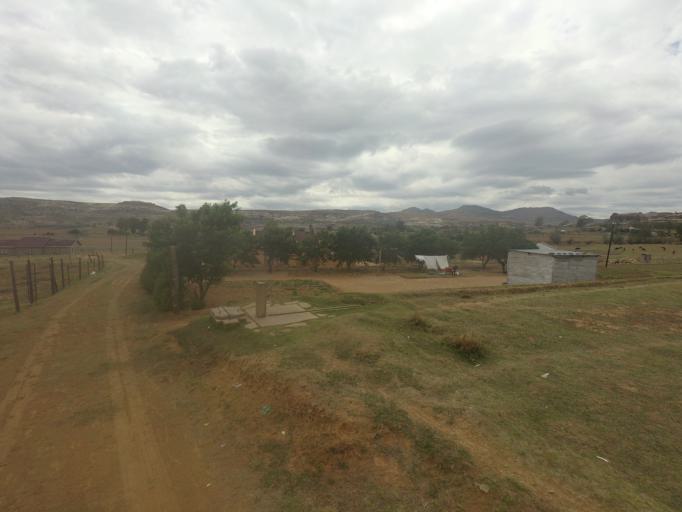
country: LS
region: Leribe
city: Leribe
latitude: -29.0273
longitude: 28.0199
